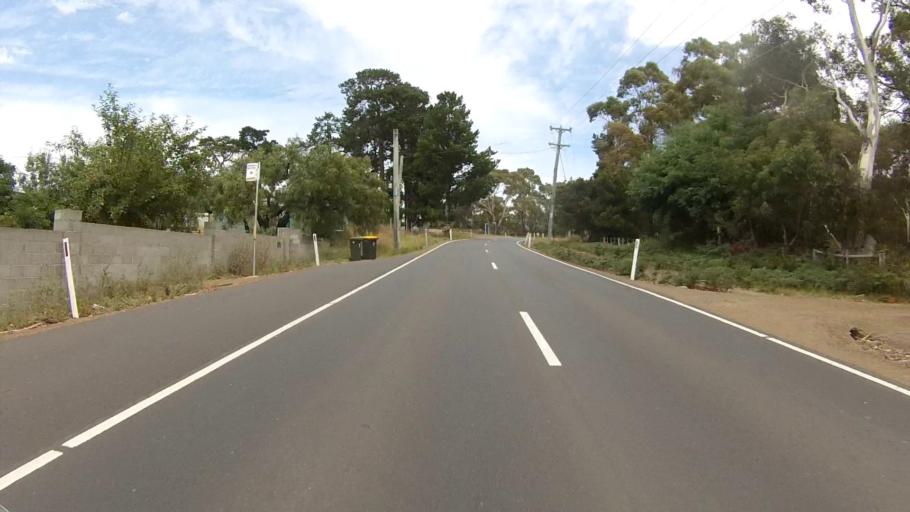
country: AU
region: Tasmania
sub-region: Clarence
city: Acton Park
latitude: -42.8669
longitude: 147.4878
